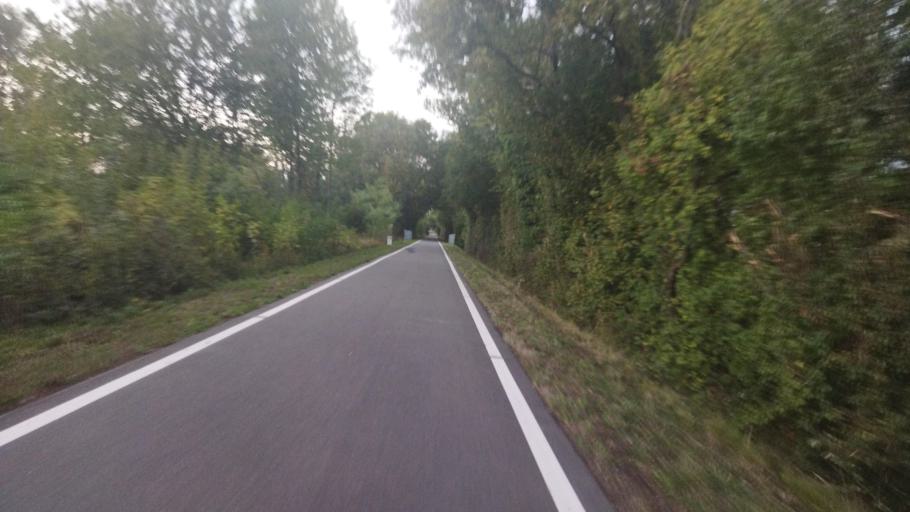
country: DE
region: North Rhine-Westphalia
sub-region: Regierungsbezirk Munster
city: Horstmar
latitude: 52.0740
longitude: 7.3208
